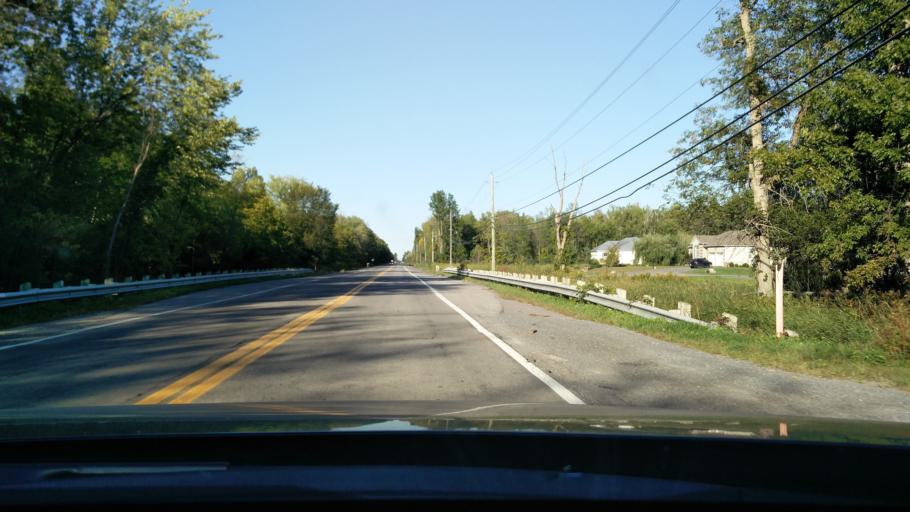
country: CA
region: Ontario
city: Bells Corners
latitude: 45.1694
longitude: -75.8773
